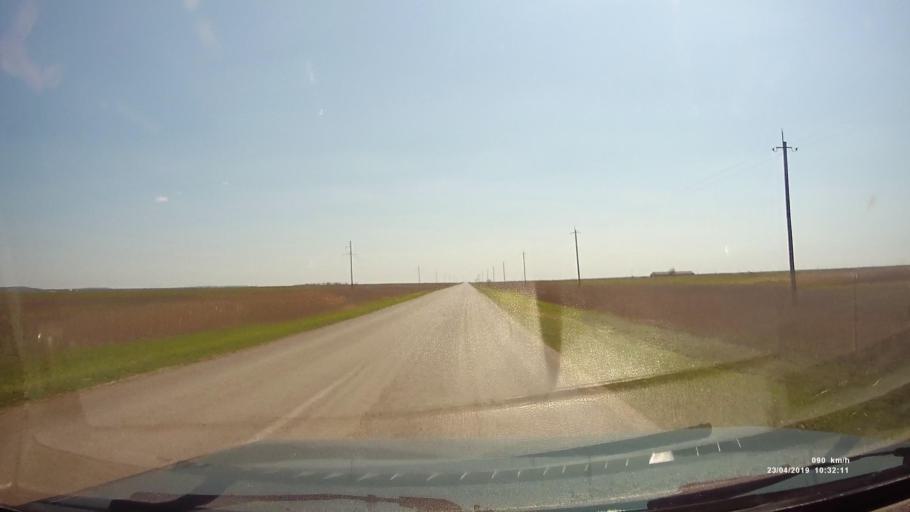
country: RU
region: Kalmykiya
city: Yashalta
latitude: 46.5818
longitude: 42.5734
